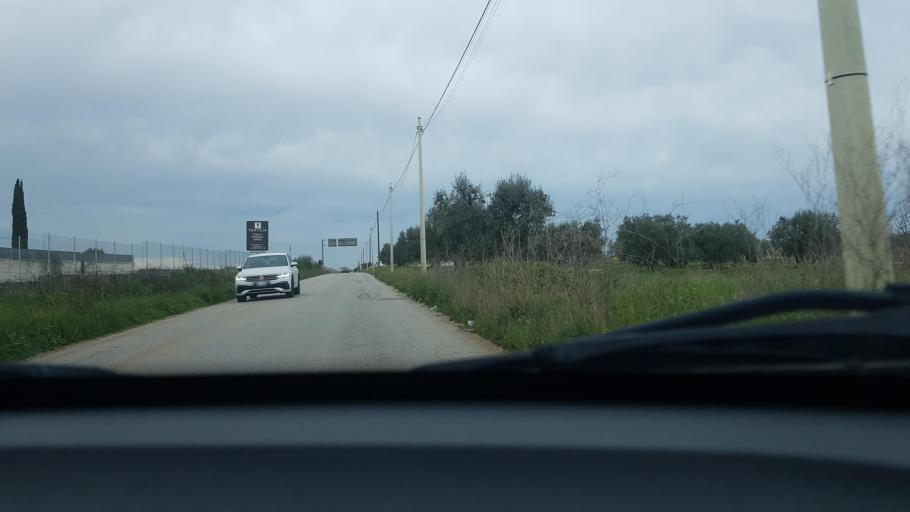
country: IT
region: Apulia
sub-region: Provincia di Bari
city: Noicattaro
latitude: 41.0337
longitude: 16.9773
